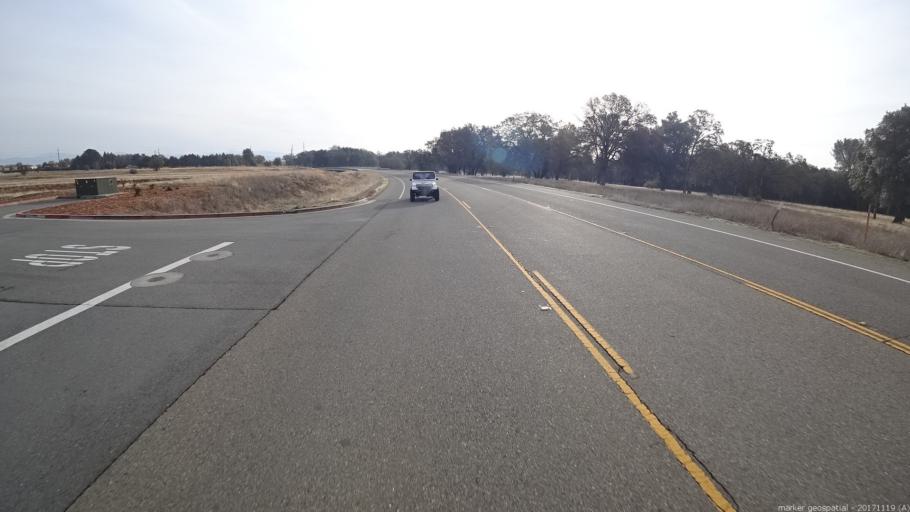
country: US
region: California
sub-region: Shasta County
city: Anderson
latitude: 40.5061
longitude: -122.3108
